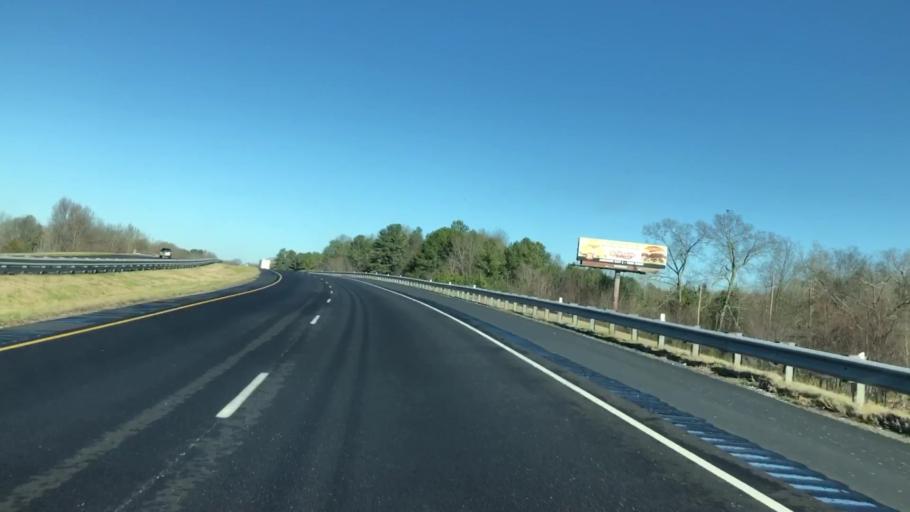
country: US
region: Alabama
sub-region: Limestone County
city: Ardmore
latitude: 34.9042
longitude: -86.9060
